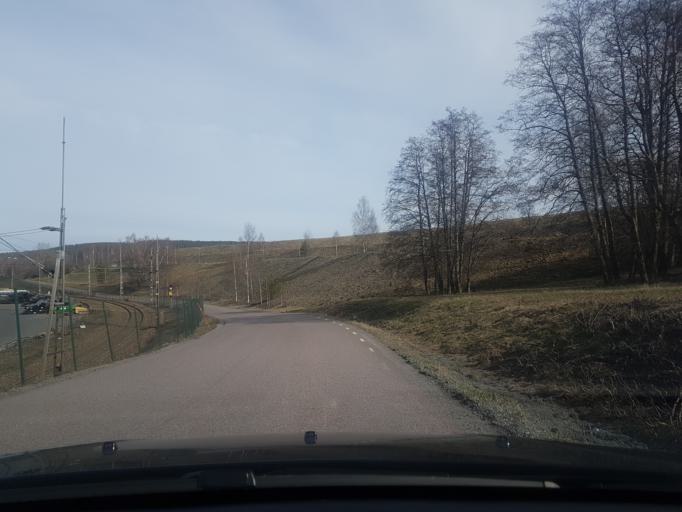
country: SE
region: Dalarna
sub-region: Borlange Kommun
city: Borlaenge
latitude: 60.4932
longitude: 15.4630
